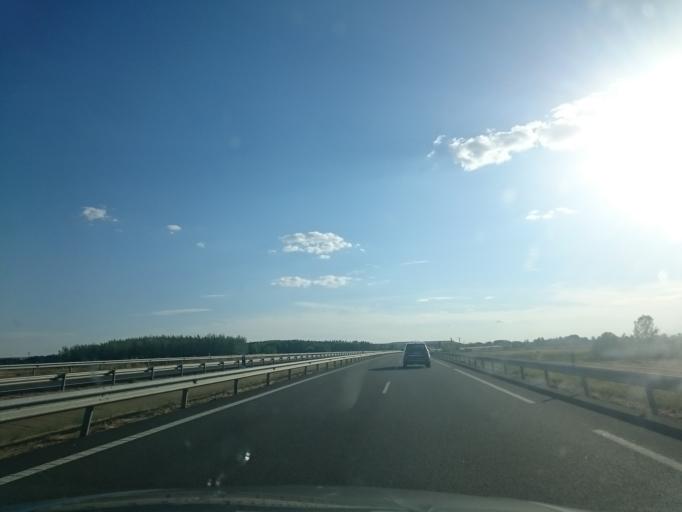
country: ES
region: Castille and Leon
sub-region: Provincia de Burgos
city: Melgar de Fernamental
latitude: 42.4104
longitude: -4.2626
